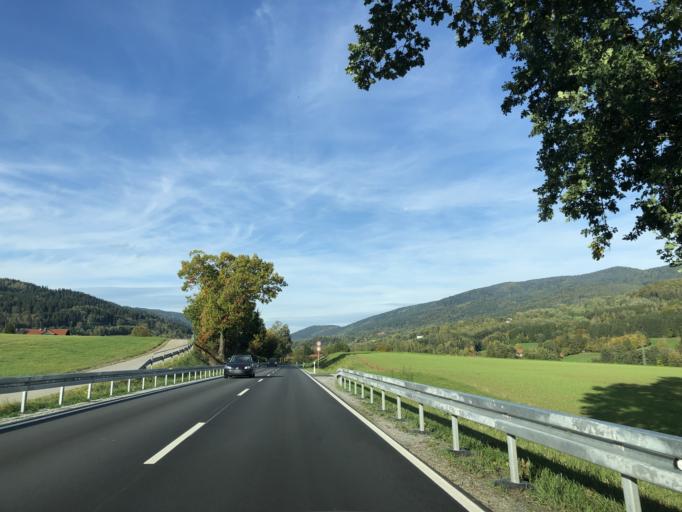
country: DE
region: Bavaria
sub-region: Lower Bavaria
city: Deggendorf
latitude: 48.8695
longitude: 12.9586
